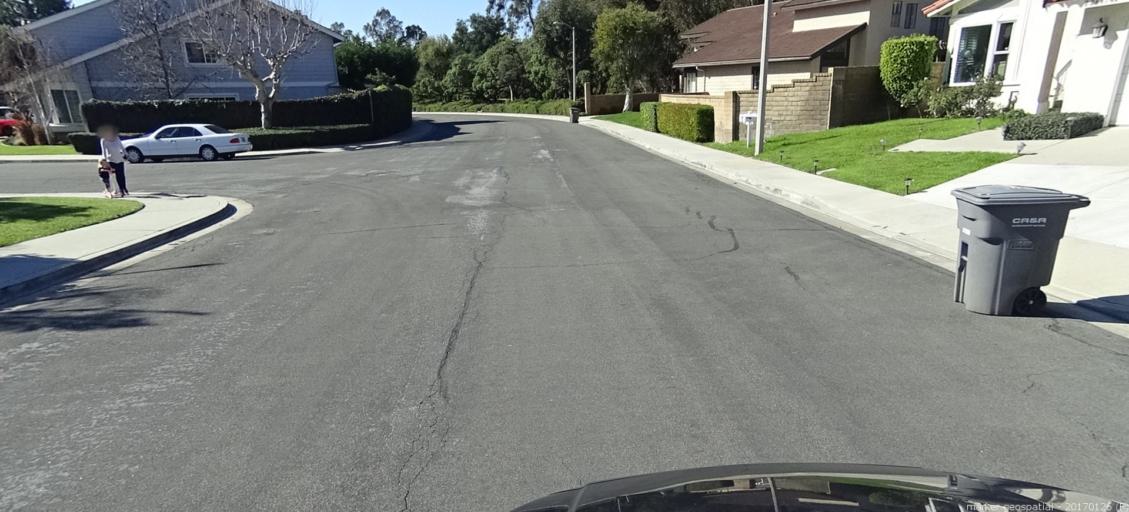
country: US
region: California
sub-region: Orange County
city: Lake Forest
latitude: 33.6338
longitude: -117.6737
